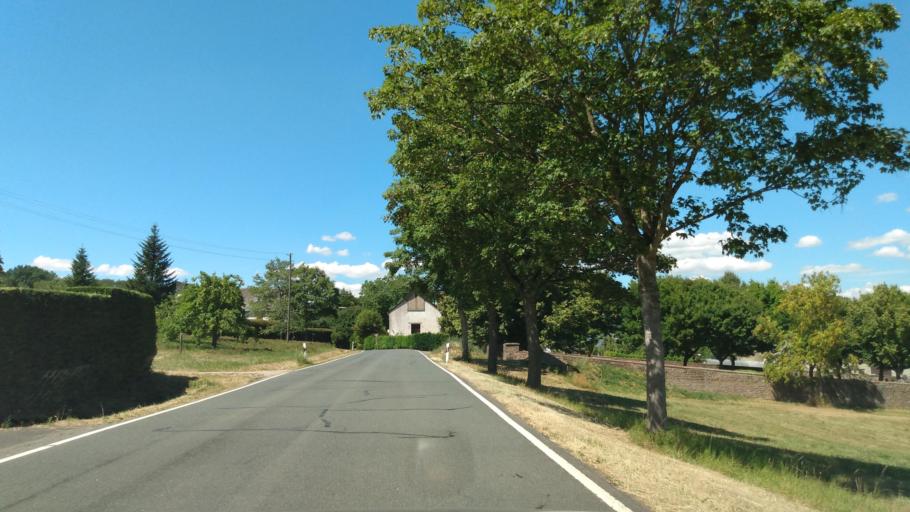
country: DE
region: Rheinland-Pfalz
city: Oberkail
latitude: 50.0340
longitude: 6.6802
